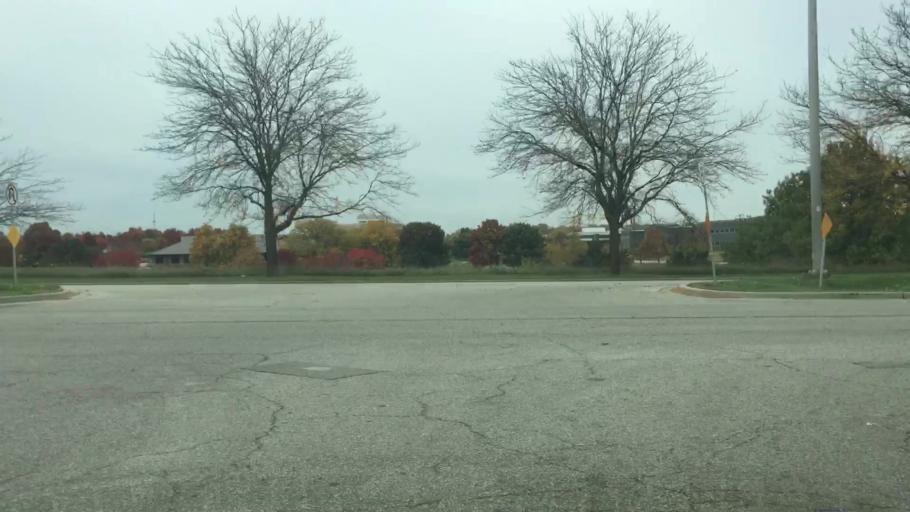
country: US
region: Kansas
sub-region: Johnson County
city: Lenexa
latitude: 38.9276
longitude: -94.7758
